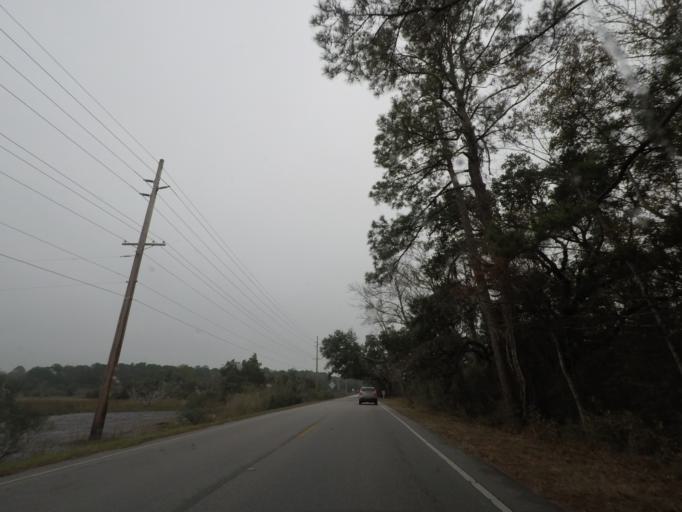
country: US
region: South Carolina
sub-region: Charleston County
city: Seabrook Island
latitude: 32.5543
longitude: -80.2801
